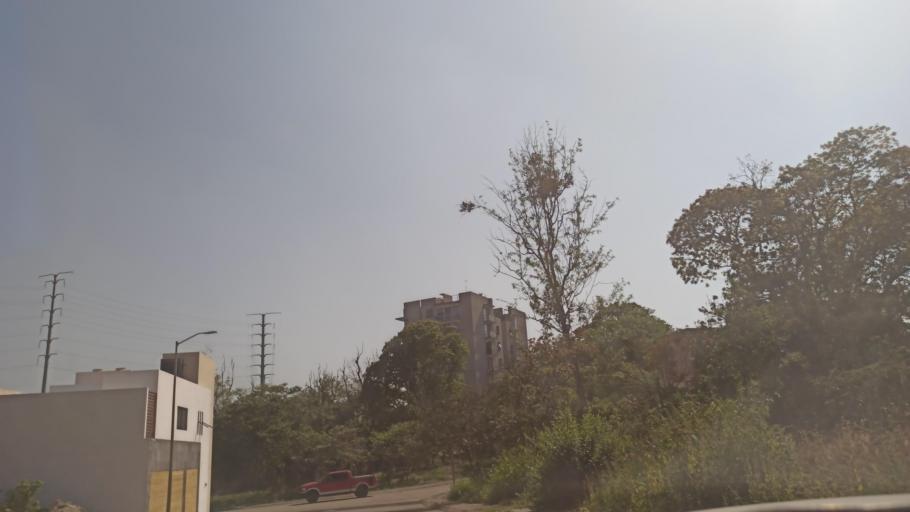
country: MX
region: Veracruz
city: El Castillo
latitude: 19.5256
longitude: -96.8653
